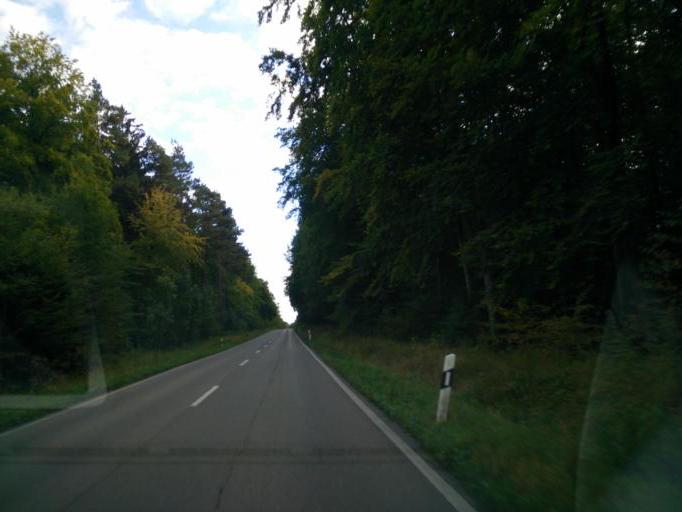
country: DE
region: Baden-Wuerttemberg
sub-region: Tuebingen Region
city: Dettenhausen
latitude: 48.5896
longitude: 9.1065
